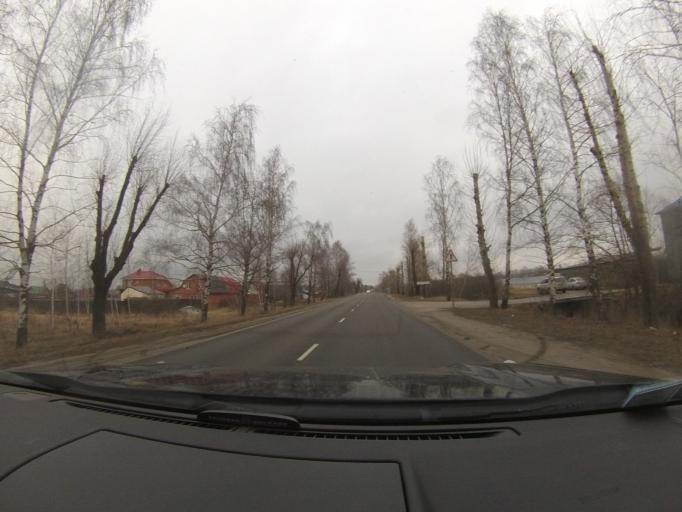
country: RU
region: Moskovskaya
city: Lopatinskiy
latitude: 55.3310
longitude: 38.7238
